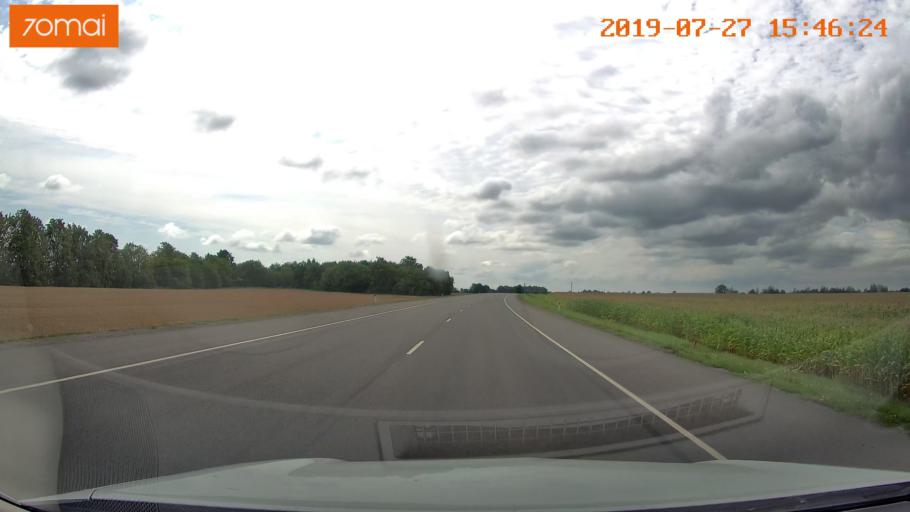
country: RU
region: Kaliningrad
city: Gusev
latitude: 54.6042
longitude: 22.1154
